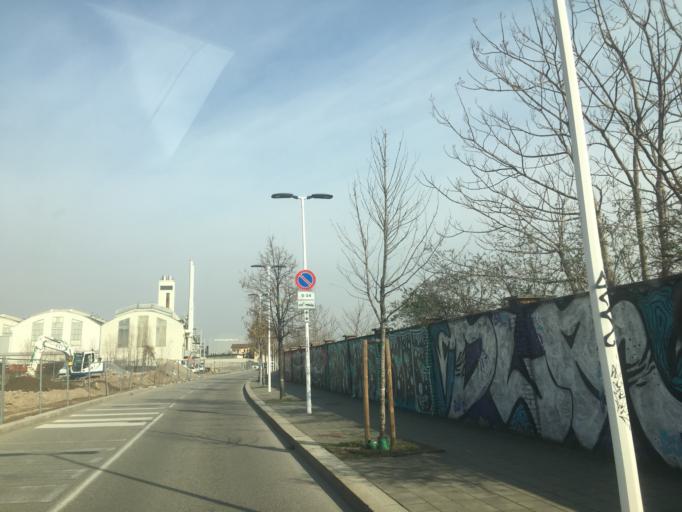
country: IT
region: Lombardy
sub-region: Citta metropolitana di Milano
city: Sesto San Giovanni
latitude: 45.5168
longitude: 9.2167
